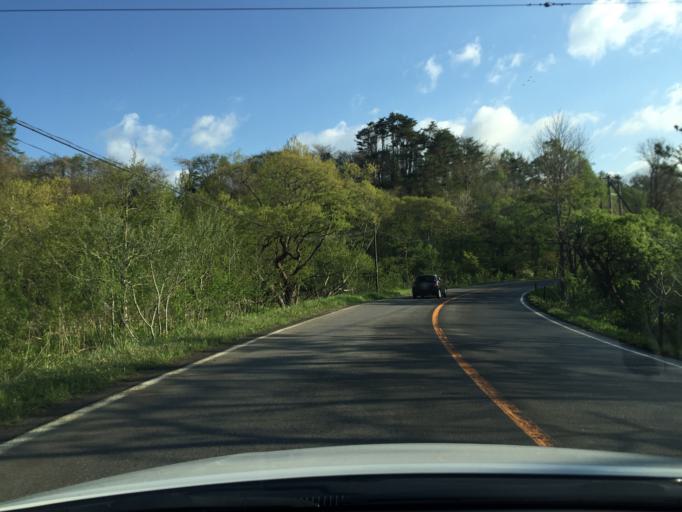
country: JP
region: Fukushima
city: Inawashiro
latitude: 37.6451
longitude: 140.0993
